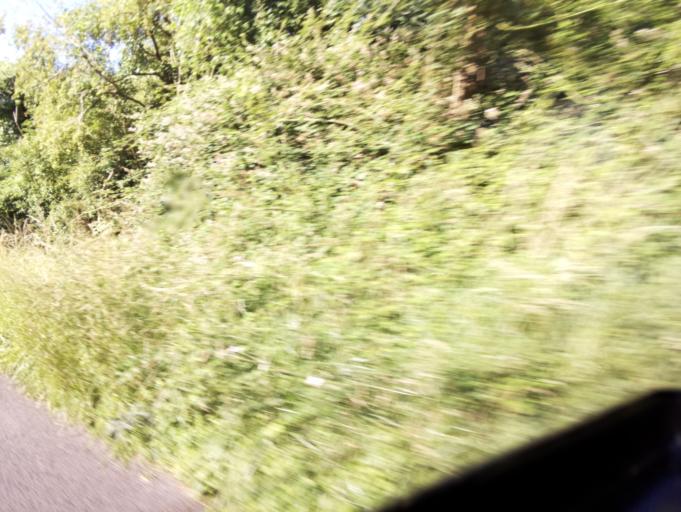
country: GB
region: England
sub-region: Gloucestershire
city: Lydbrook
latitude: 51.8530
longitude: -2.5775
